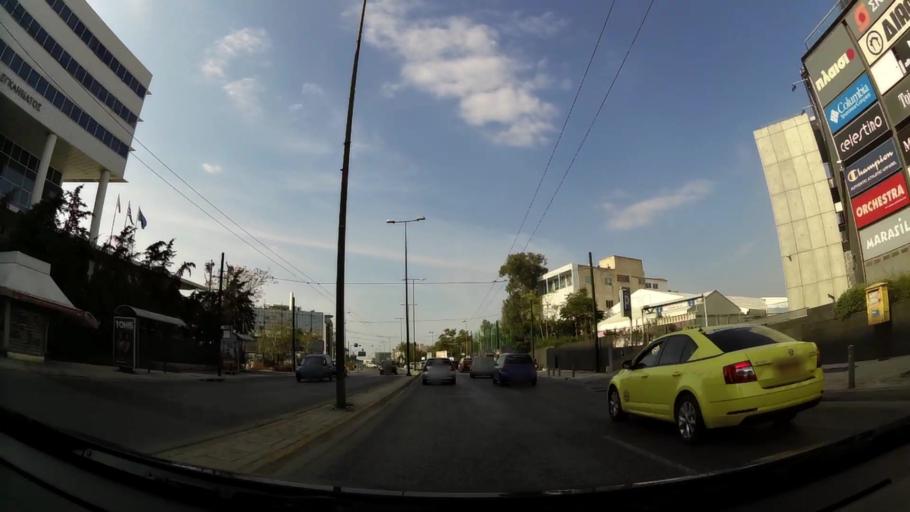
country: GR
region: Attica
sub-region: Nomarchia Athinas
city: Tavros
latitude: 37.9695
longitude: 23.7007
